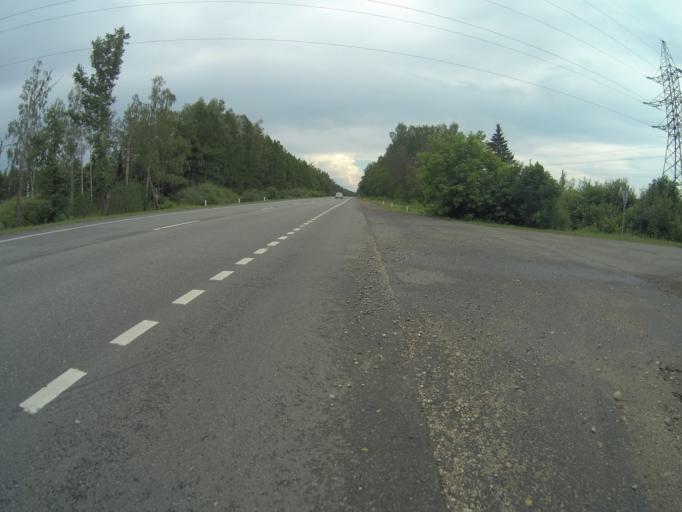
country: RU
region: Vladimir
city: Kameshkovo
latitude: 56.1972
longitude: 40.8619
